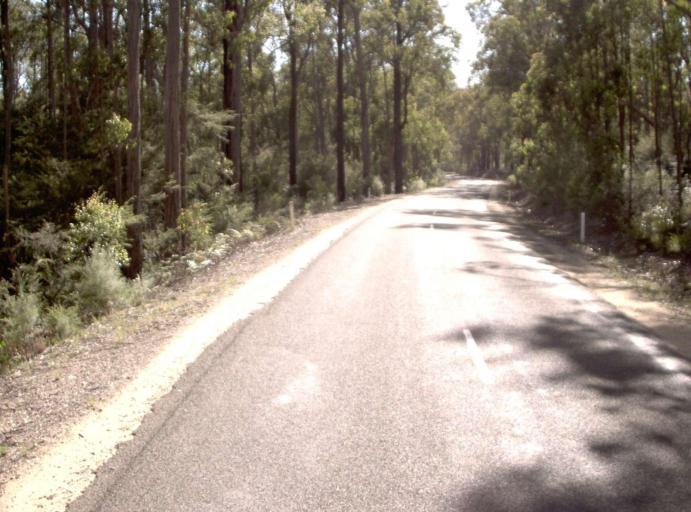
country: AU
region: Victoria
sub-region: East Gippsland
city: Lakes Entrance
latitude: -37.6605
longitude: 148.0829
